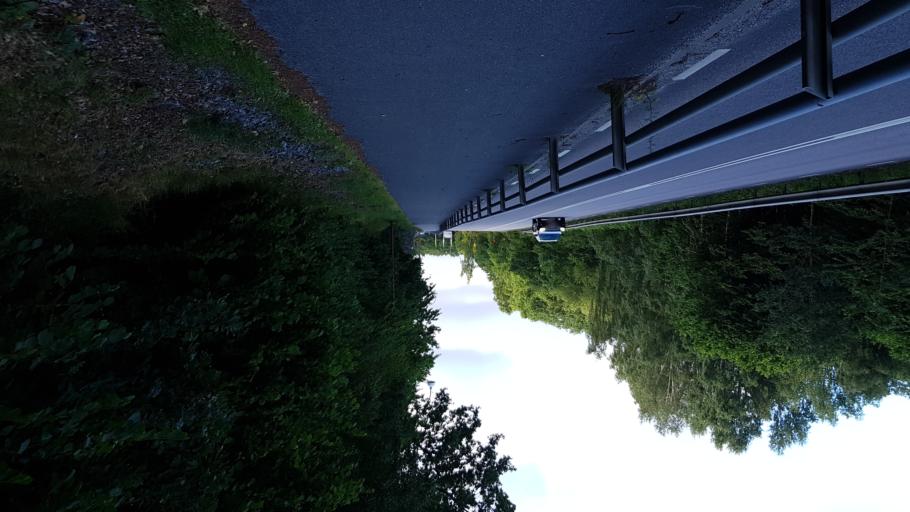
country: SE
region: Vaestra Goetaland
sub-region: Harryda Kommun
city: Molnlycke
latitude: 57.6669
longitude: 12.0918
